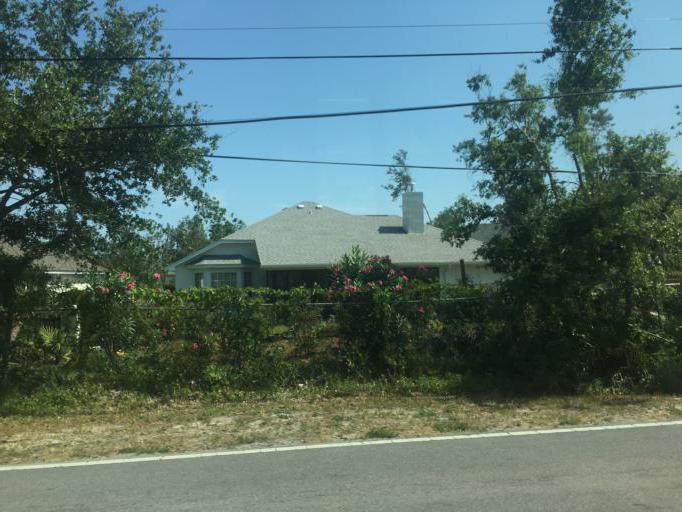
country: US
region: Florida
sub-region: Bay County
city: Upper Grand Lagoon
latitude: 30.1588
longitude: -85.7326
